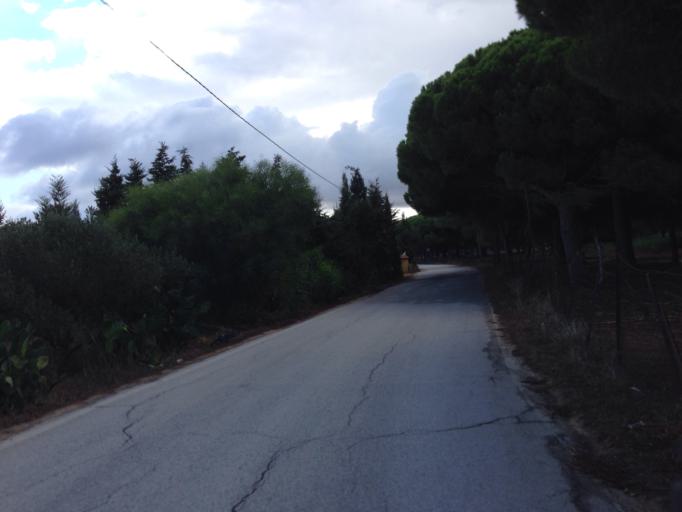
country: ES
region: Andalusia
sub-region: Provincia de Cadiz
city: Conil de la Frontera
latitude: 36.3113
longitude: -6.1164
